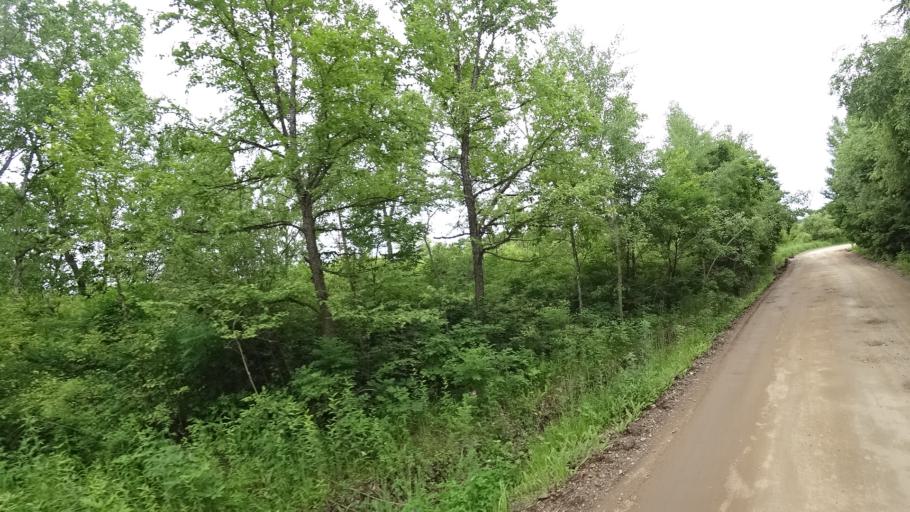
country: RU
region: Primorskiy
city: Arsen'yev
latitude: 44.1912
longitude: 133.3105
